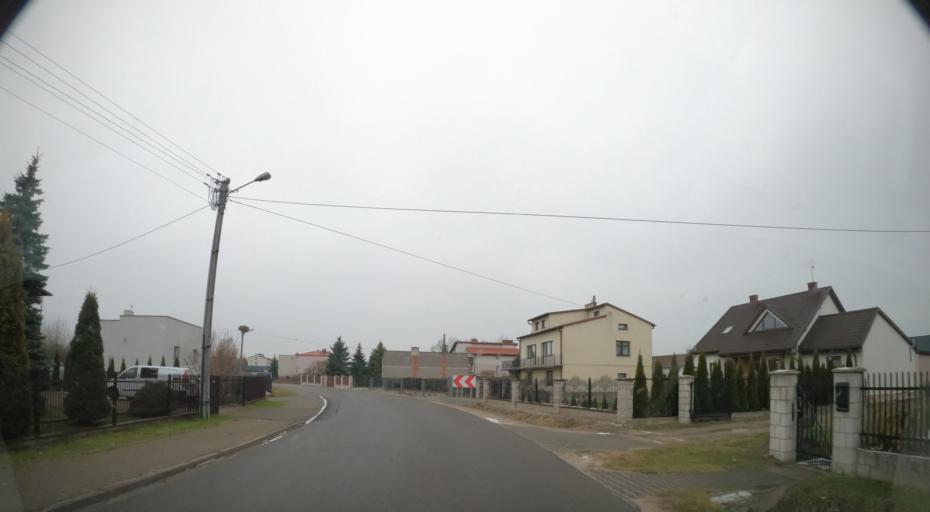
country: PL
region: Masovian Voivodeship
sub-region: Powiat radomski
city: Skaryszew
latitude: 51.3804
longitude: 21.2303
